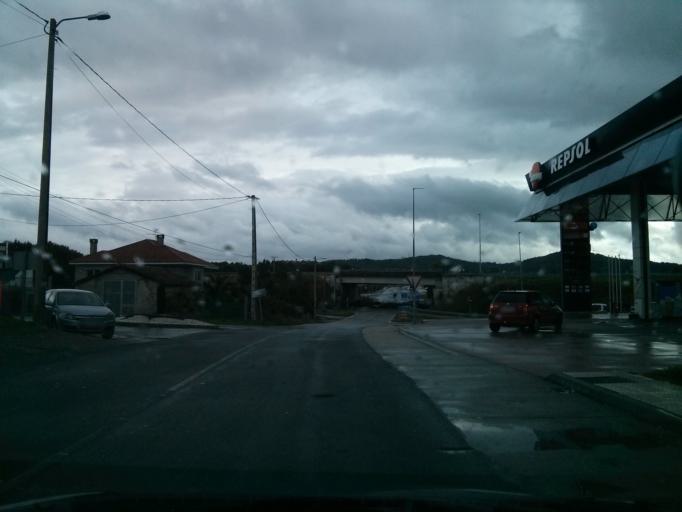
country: ES
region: Galicia
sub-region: Provincia de Ourense
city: Taboadela
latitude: 42.2510
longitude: -7.8642
